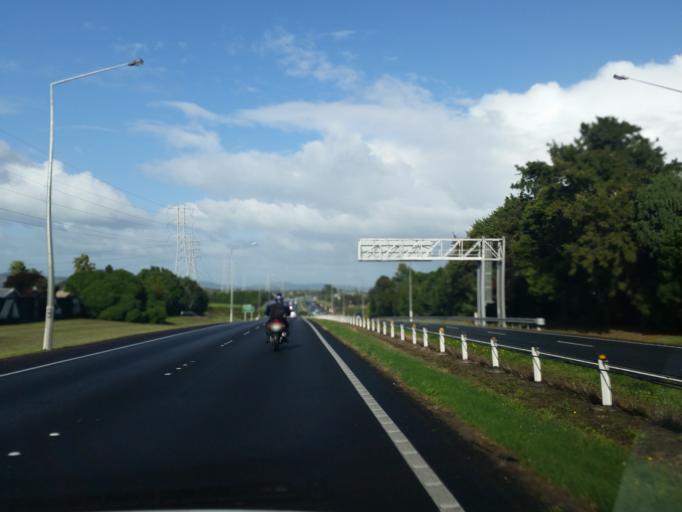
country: NZ
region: Auckland
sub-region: Auckland
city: Takanini
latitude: -37.0495
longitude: 174.9163
